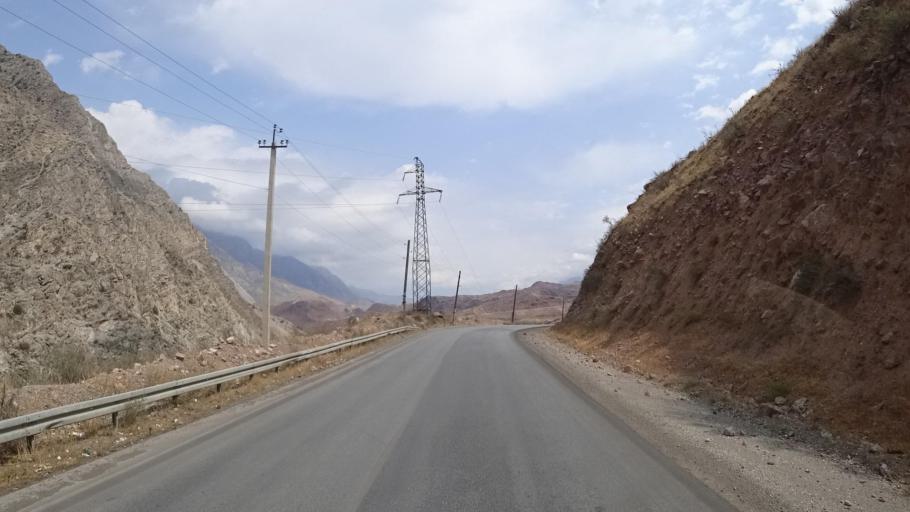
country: KG
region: Jalal-Abad
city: Toktogul
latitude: 41.6126
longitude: 72.6090
